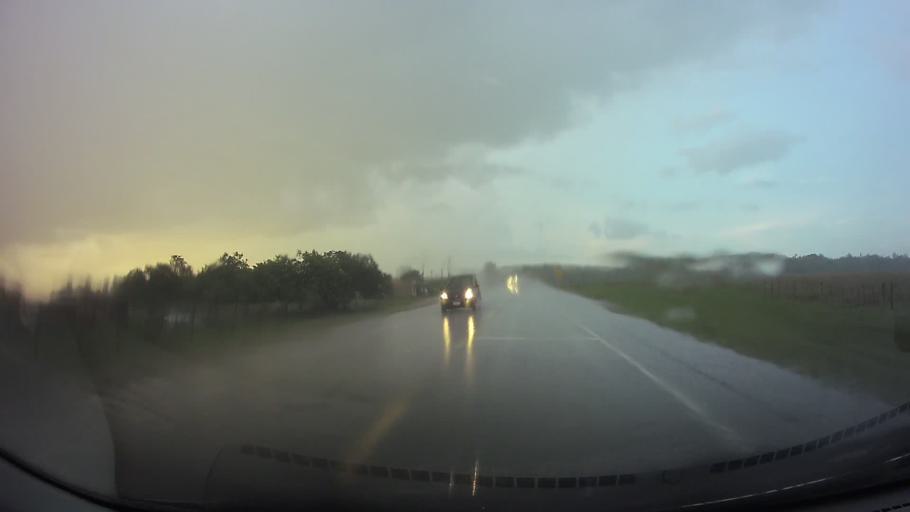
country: PY
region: Paraguari
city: Paraguari
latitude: -25.6322
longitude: -57.1566
